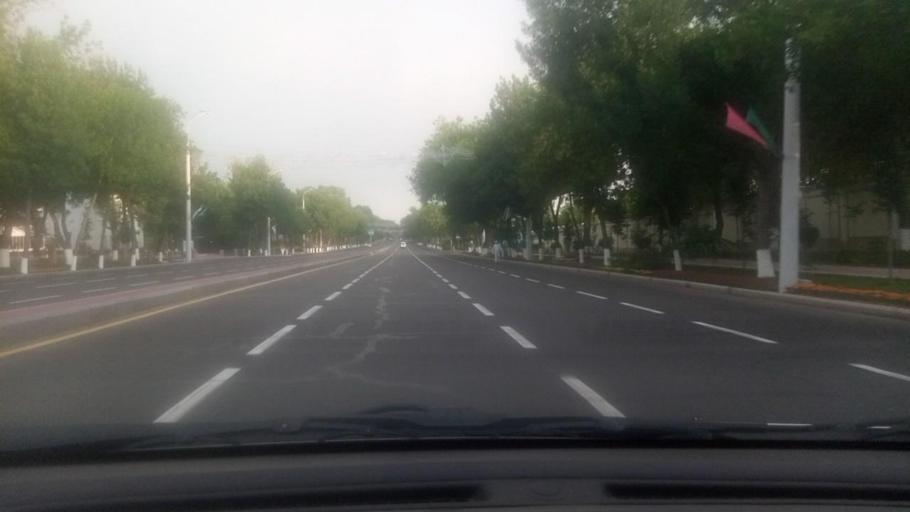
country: UZ
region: Toshkent
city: Salor
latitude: 41.3347
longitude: 69.3453
